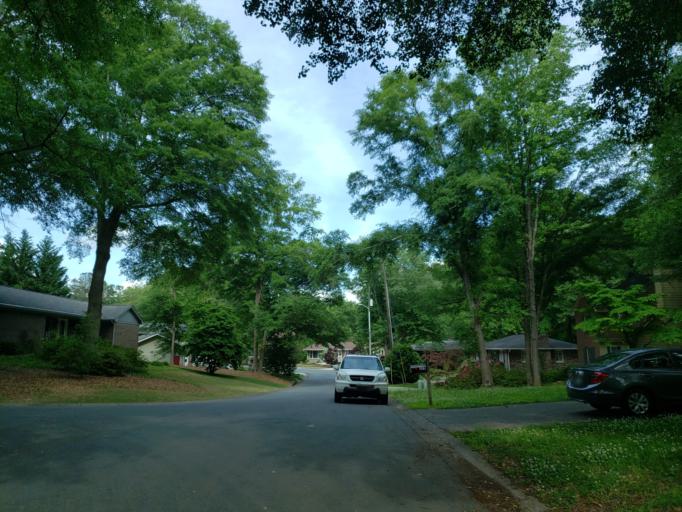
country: US
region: Georgia
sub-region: Cobb County
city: Marietta
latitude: 33.9443
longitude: -84.5734
